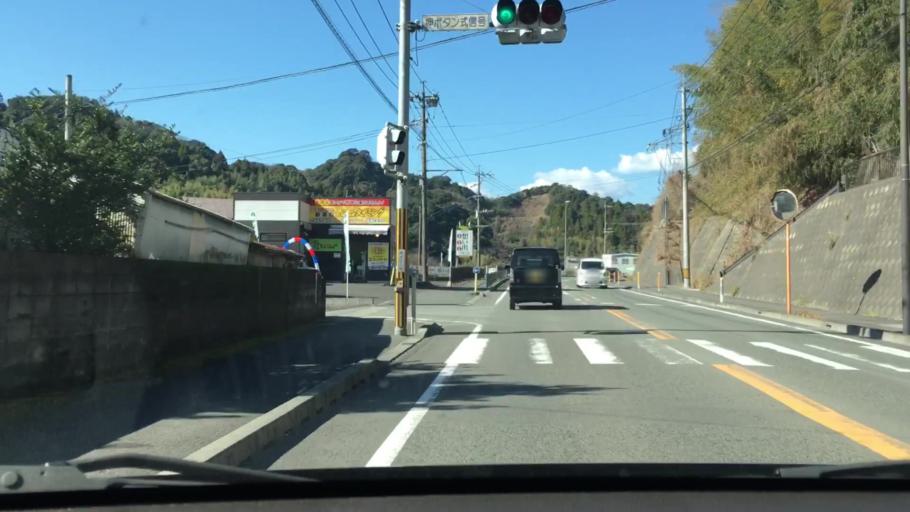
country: JP
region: Kagoshima
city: Kagoshima-shi
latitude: 31.6347
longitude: 130.5217
